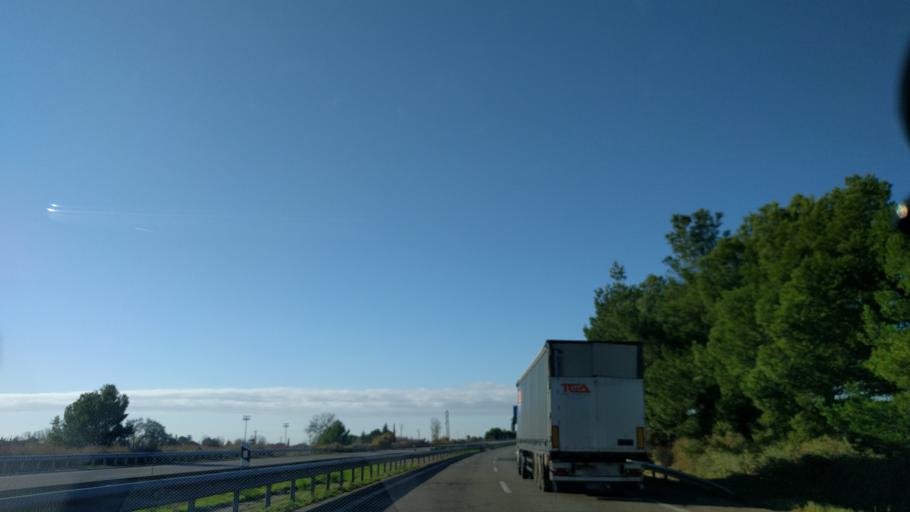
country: ES
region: Catalonia
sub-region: Provincia de Lleida
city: Alpicat
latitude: 41.6521
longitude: 0.5738
